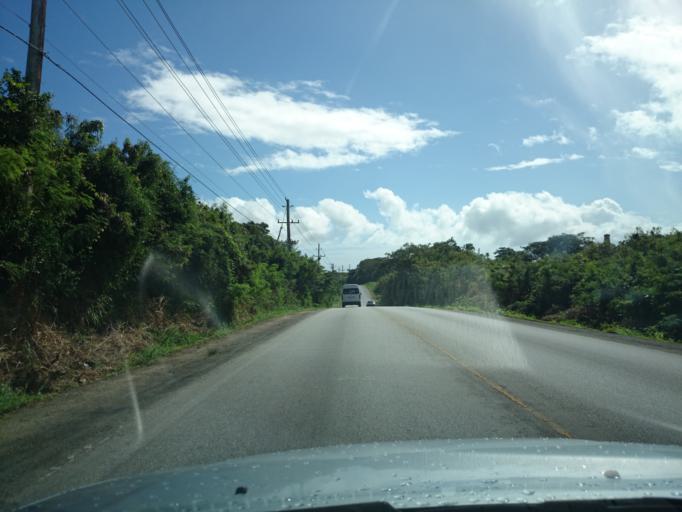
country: BB
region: Saint James
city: Holetown
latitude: 13.2065
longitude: -59.6175
